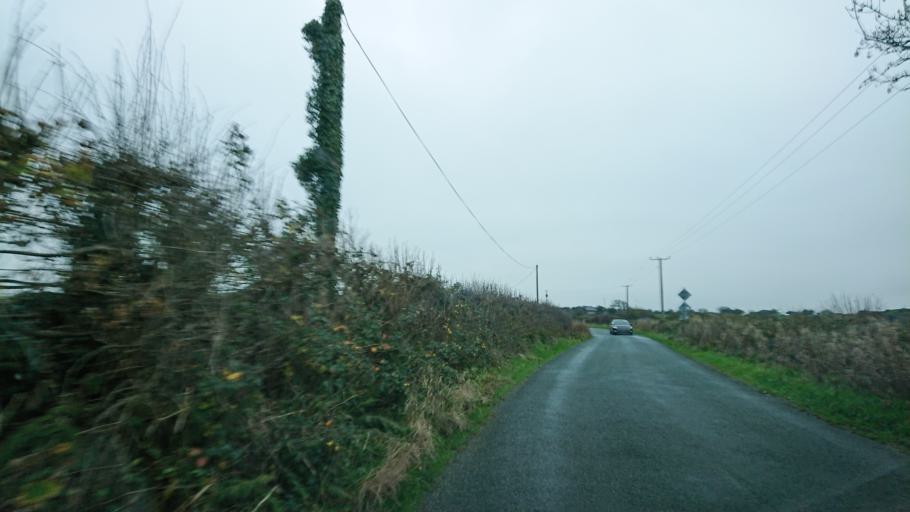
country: IE
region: Munster
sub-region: Waterford
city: Dunmore East
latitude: 52.1591
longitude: -7.0622
